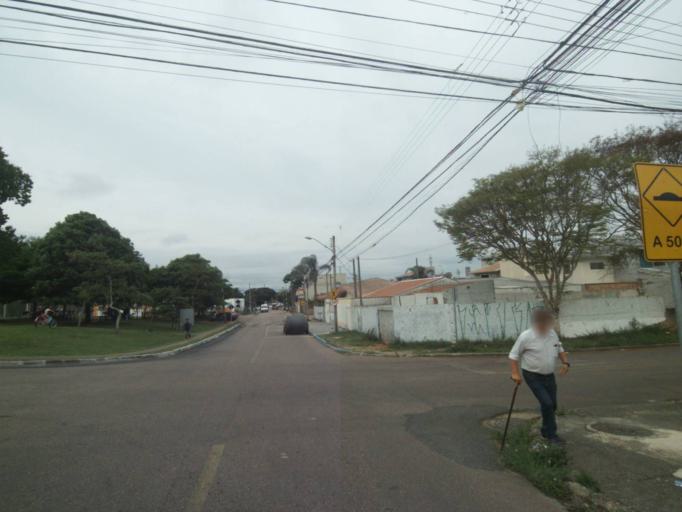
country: BR
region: Parana
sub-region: Sao Jose Dos Pinhais
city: Sao Jose dos Pinhais
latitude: -25.5482
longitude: -49.2641
